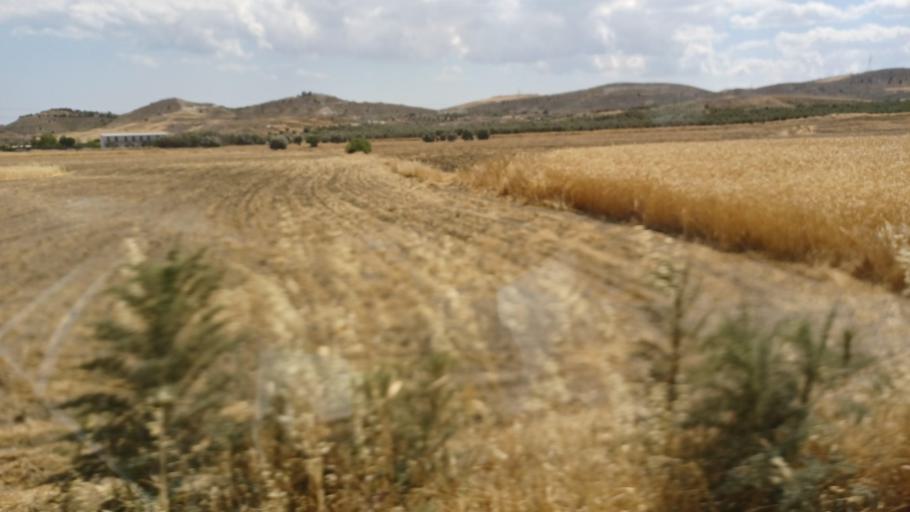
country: CY
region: Larnaka
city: Troulloi
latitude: 35.0022
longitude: 33.5840
